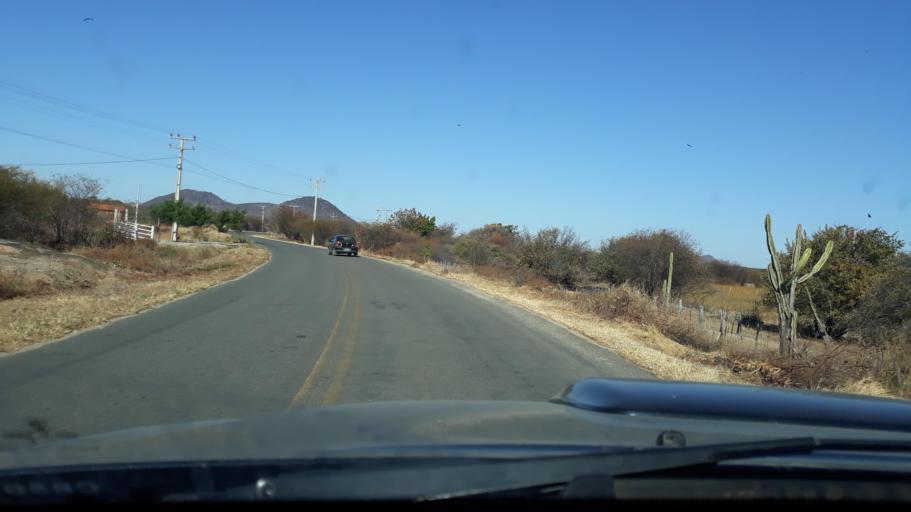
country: BR
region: Bahia
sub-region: Guanambi
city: Guanambi
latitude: -14.0193
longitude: -42.8647
